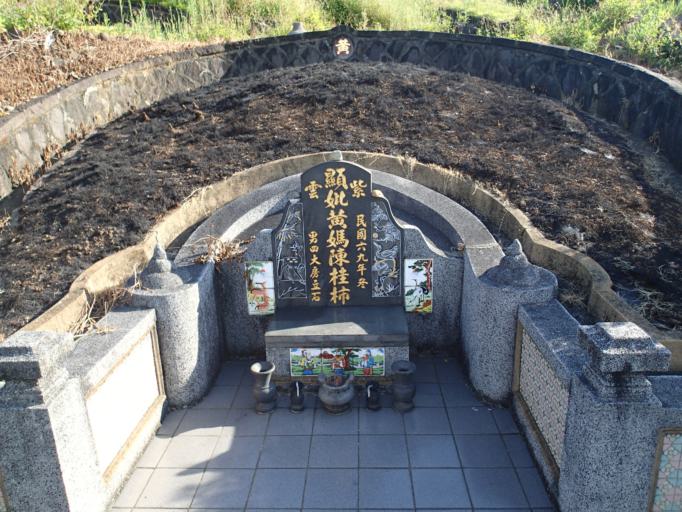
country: TW
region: Taipei
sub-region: Taipei
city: Banqiao
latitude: 25.1091
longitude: 121.4397
